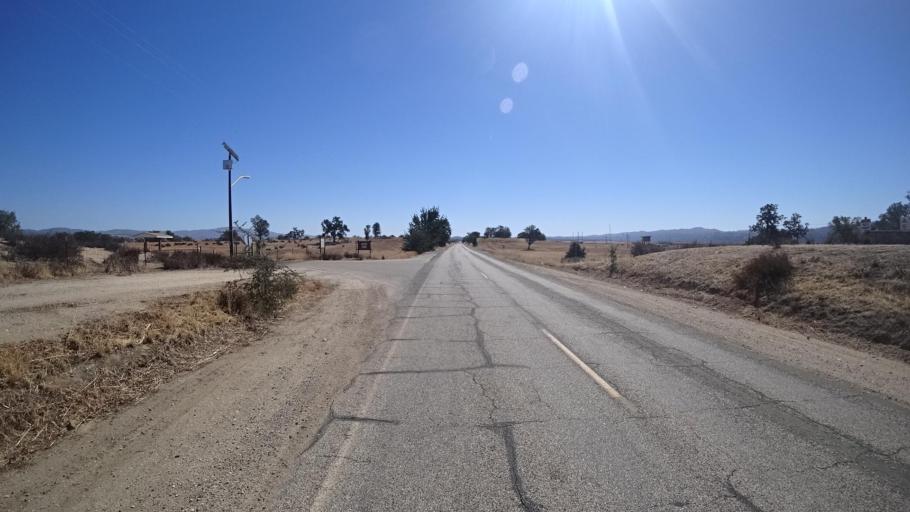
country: US
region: California
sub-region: Monterey County
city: King City
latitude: 35.9586
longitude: -121.1585
